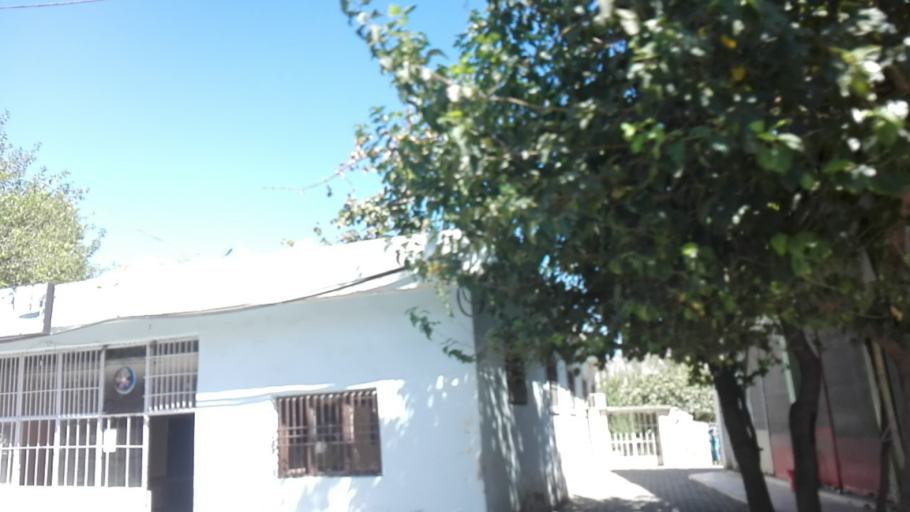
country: TR
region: Batman
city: Hasankeyf
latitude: 37.7130
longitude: 41.4143
